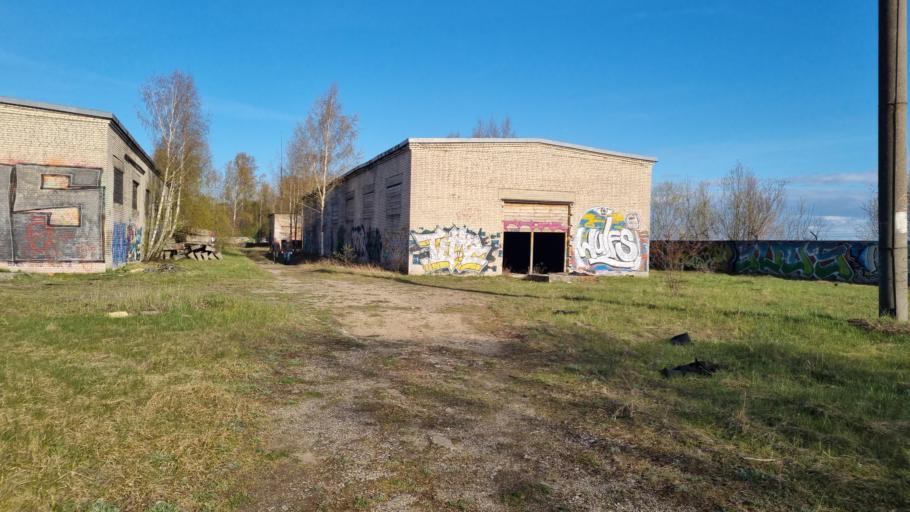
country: LV
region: Riga
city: Daugavgriva
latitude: 57.0603
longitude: 24.0411
